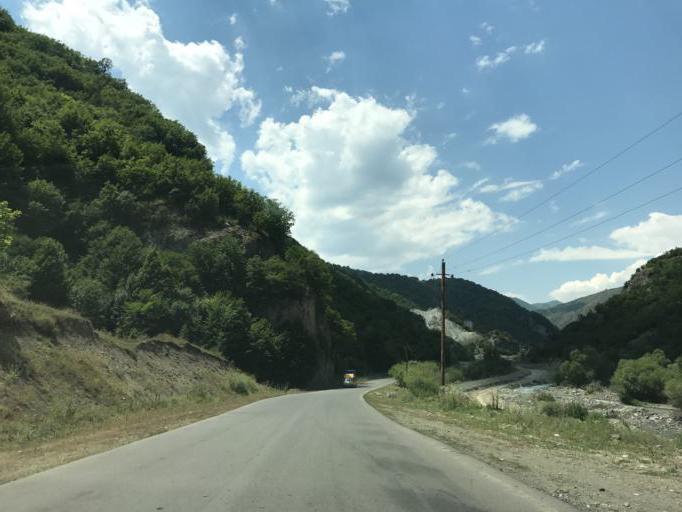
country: AZ
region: Kalbacar Rayonu
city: Kerbakhiar
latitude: 40.2276
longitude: 46.1397
